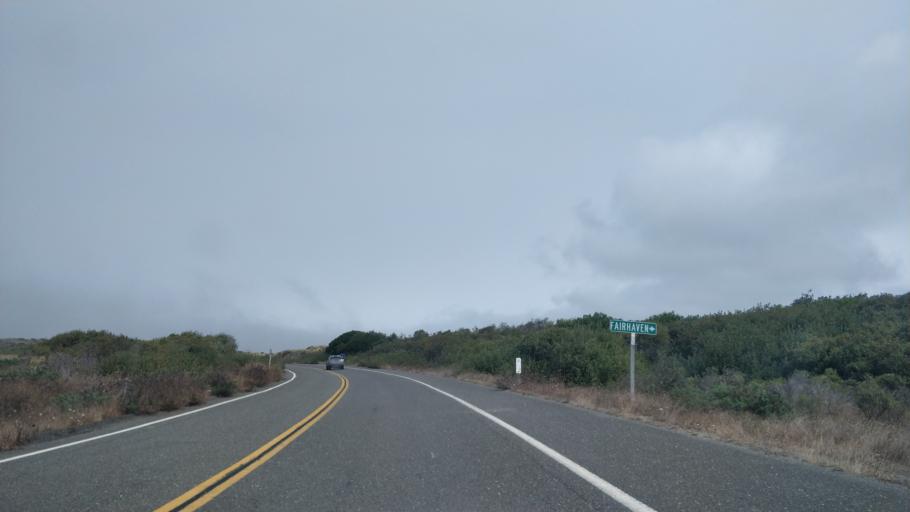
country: US
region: California
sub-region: Humboldt County
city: Bayview
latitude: 40.7804
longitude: -124.2071
